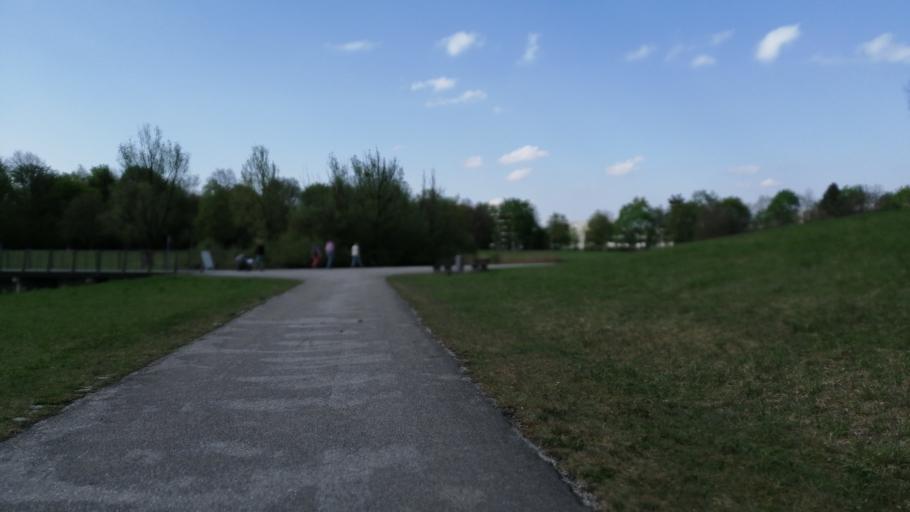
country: DE
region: Bavaria
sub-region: Upper Bavaria
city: Unterhaching
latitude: 48.0987
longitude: 11.6208
